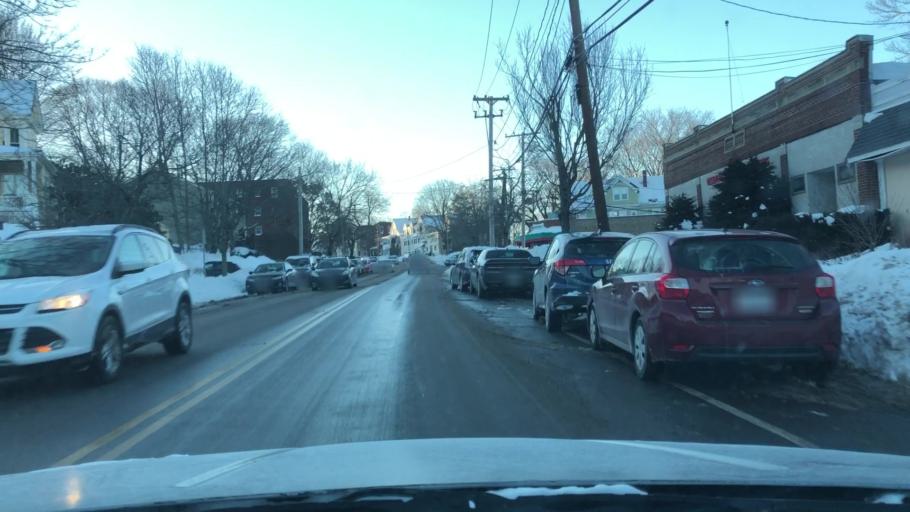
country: US
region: Massachusetts
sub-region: Middlesex County
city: Arlington
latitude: 42.4237
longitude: -71.1763
